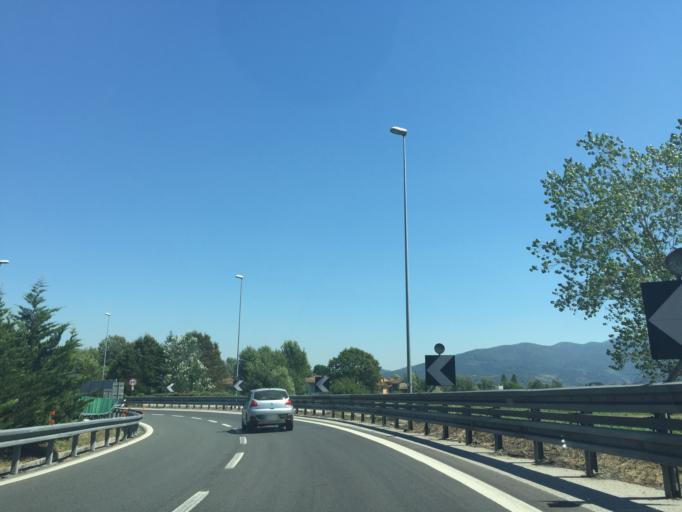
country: IT
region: Tuscany
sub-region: Provincia di Lucca
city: Lucca
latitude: 43.8320
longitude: 10.4751
